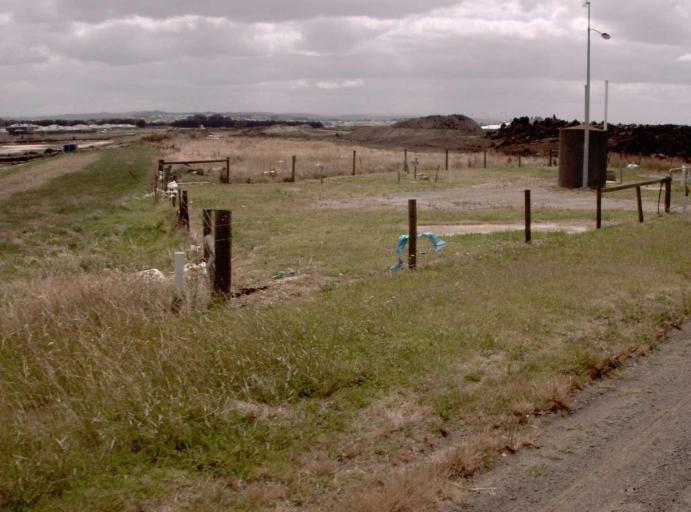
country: AU
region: Victoria
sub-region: Casey
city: Cranbourne East
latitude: -38.0880
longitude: 145.3219
